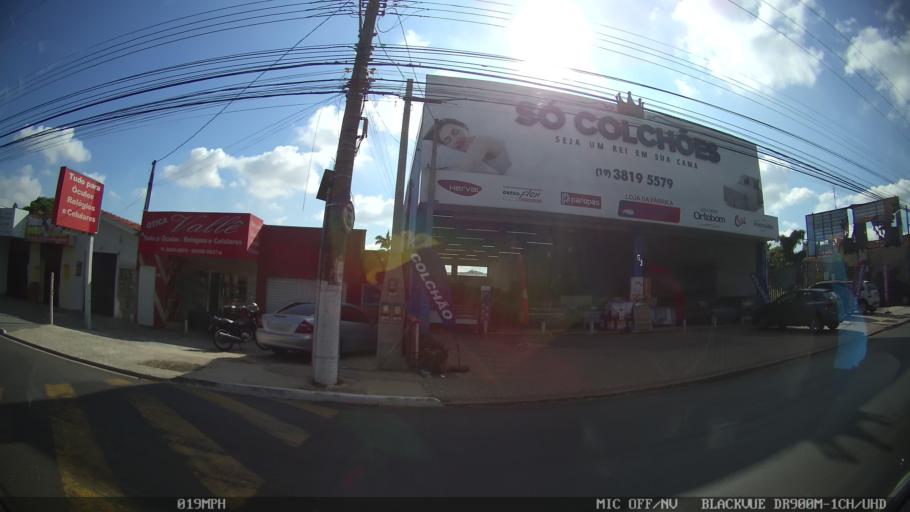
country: BR
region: Sao Paulo
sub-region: Hortolandia
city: Hortolandia
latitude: -22.8623
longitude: -47.2203
